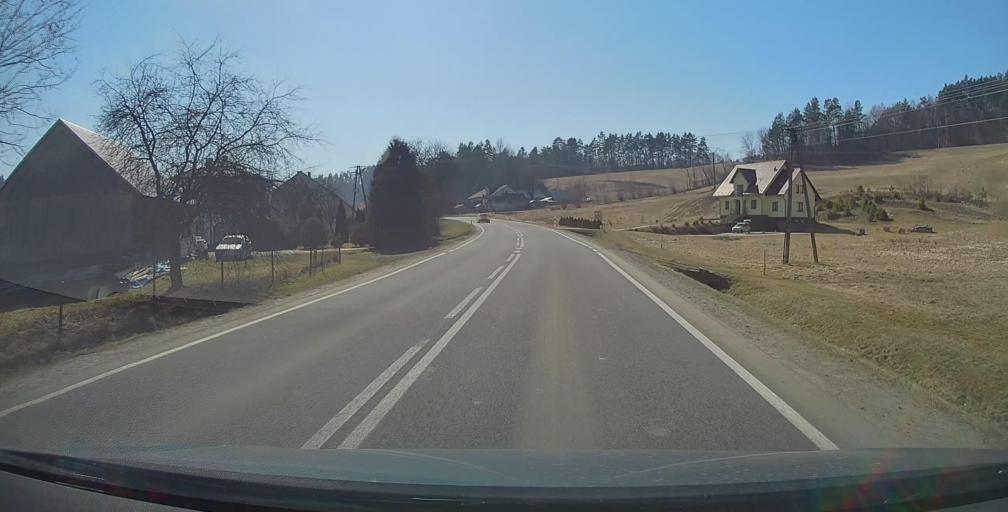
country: PL
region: Subcarpathian Voivodeship
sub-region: Powiat przemyski
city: Bircza
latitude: 49.6762
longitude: 22.4332
